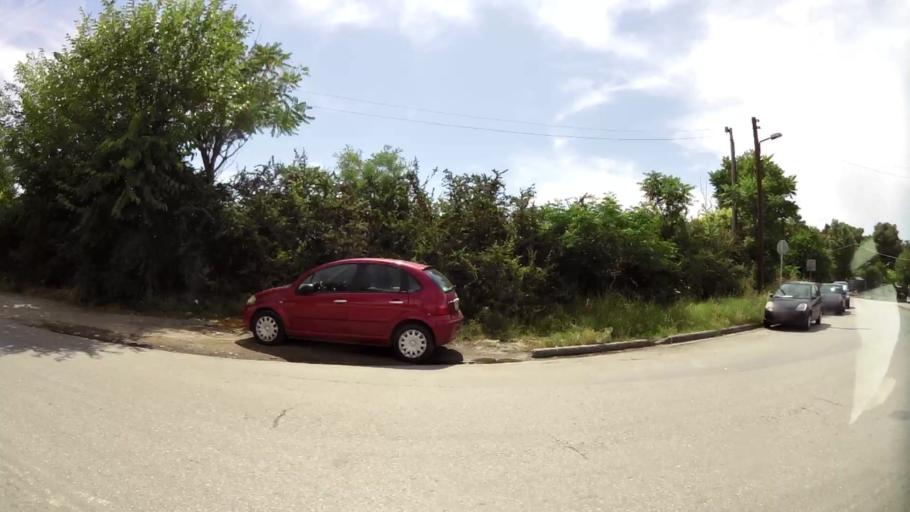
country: GR
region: Central Macedonia
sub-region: Nomos Thessalonikis
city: Pylaia
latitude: 40.5953
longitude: 22.9715
